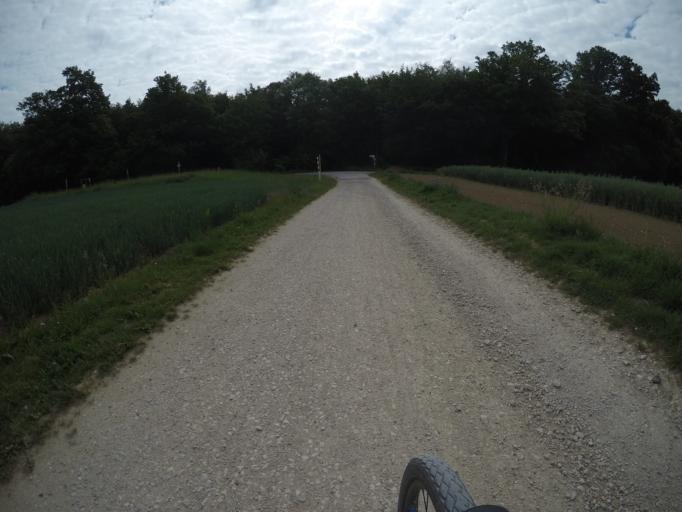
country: DE
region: Baden-Wuerttemberg
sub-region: Regierungsbezirk Stuttgart
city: Oberboihingen
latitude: 48.6501
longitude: 9.3944
